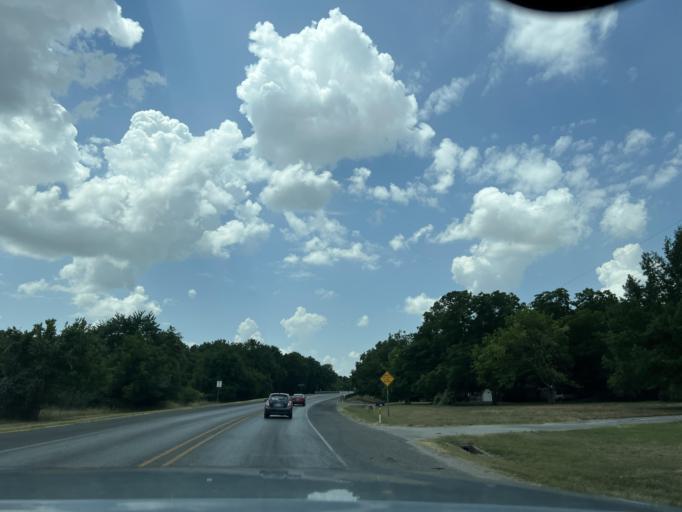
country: US
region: Texas
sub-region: Parker County
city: Springtown
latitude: 32.9575
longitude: -97.6830
